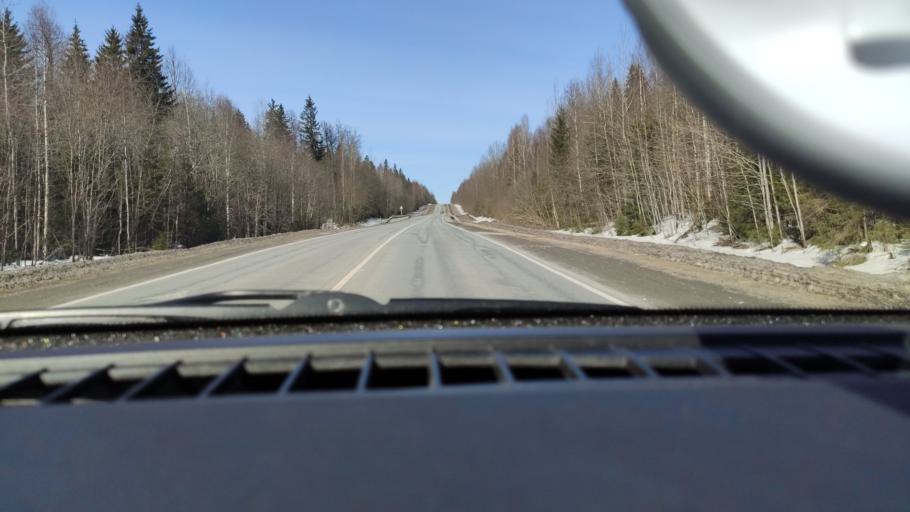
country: RU
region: Perm
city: Perm
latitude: 58.1691
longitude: 56.2363
